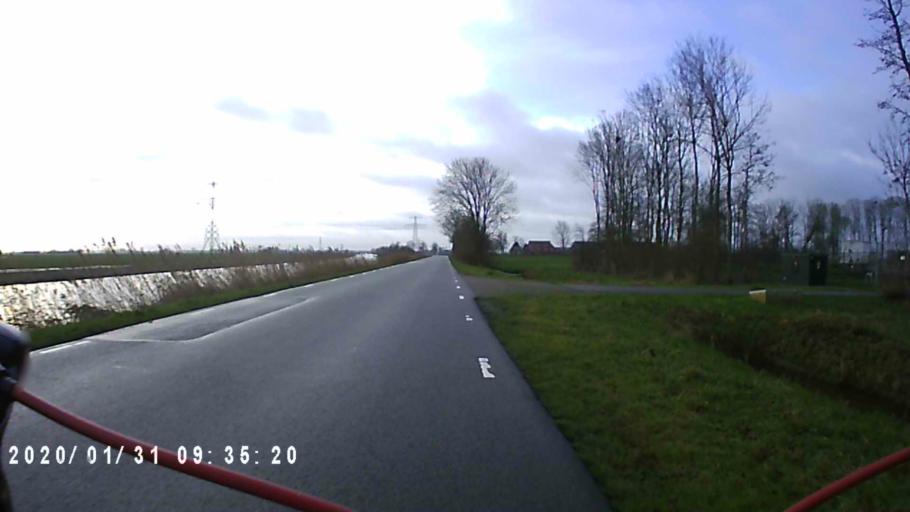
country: NL
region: Groningen
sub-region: Gemeente Winsum
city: Winsum
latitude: 53.3028
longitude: 6.4807
